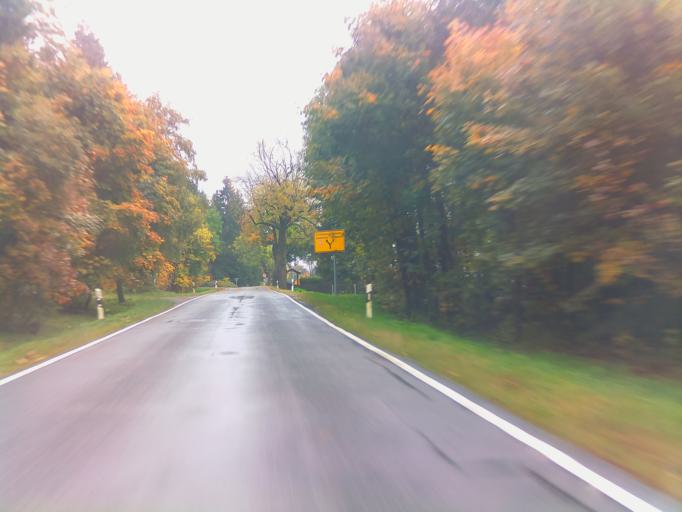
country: DE
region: Thuringia
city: Wurzbach
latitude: 50.4315
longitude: 11.5062
